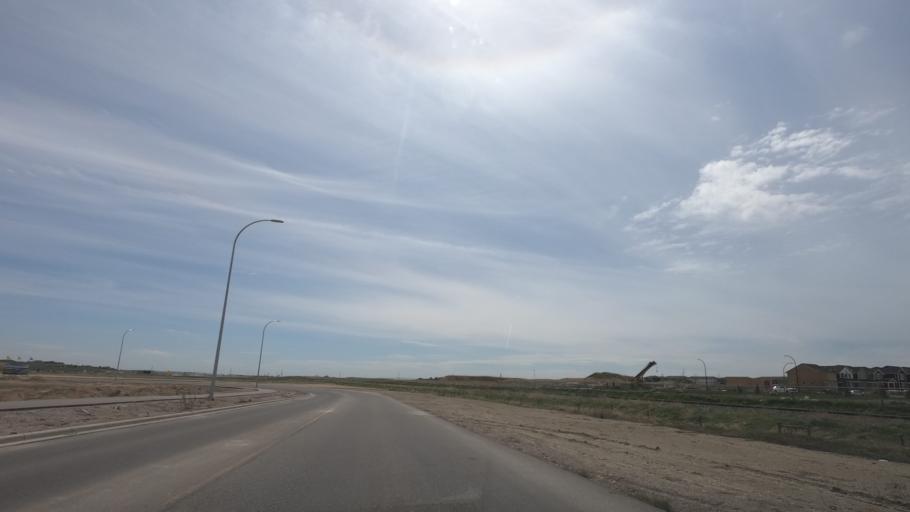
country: CA
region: Alberta
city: Airdrie
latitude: 51.2538
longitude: -114.0076
